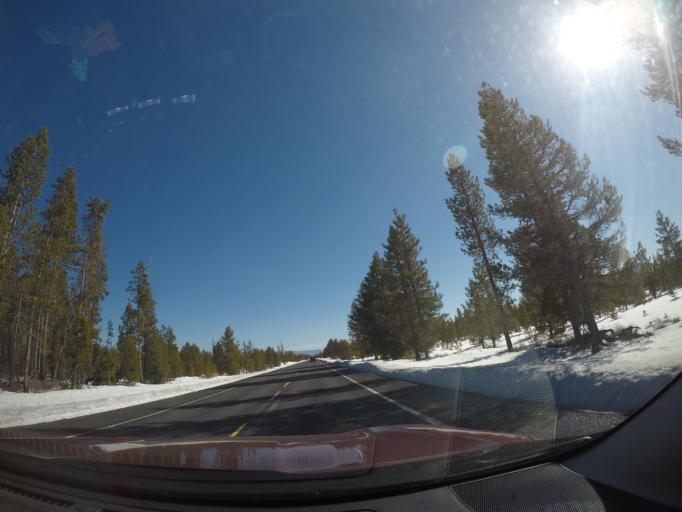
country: US
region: Oregon
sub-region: Deschutes County
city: Three Rivers
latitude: 43.8858
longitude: -121.5774
